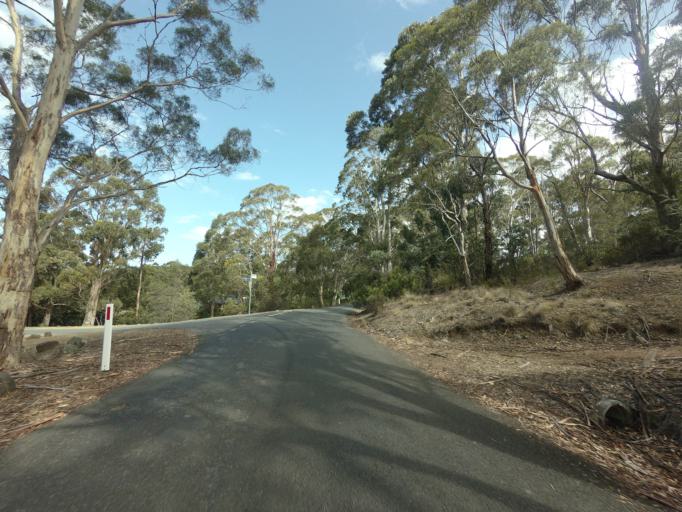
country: AU
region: Tasmania
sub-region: Hobart
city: Dynnyrne
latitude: -42.9228
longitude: 147.2876
